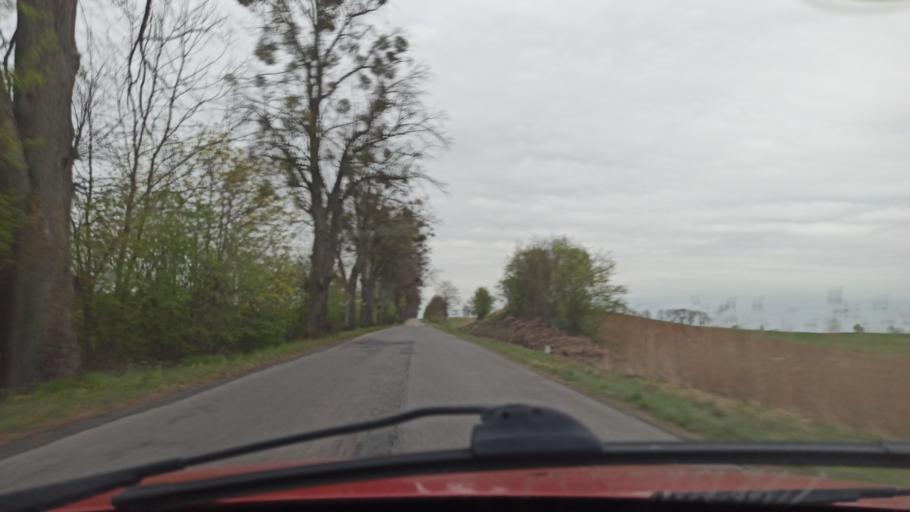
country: PL
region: Pomeranian Voivodeship
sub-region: Powiat kwidzynski
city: Gardeja
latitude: 53.5712
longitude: 18.9873
